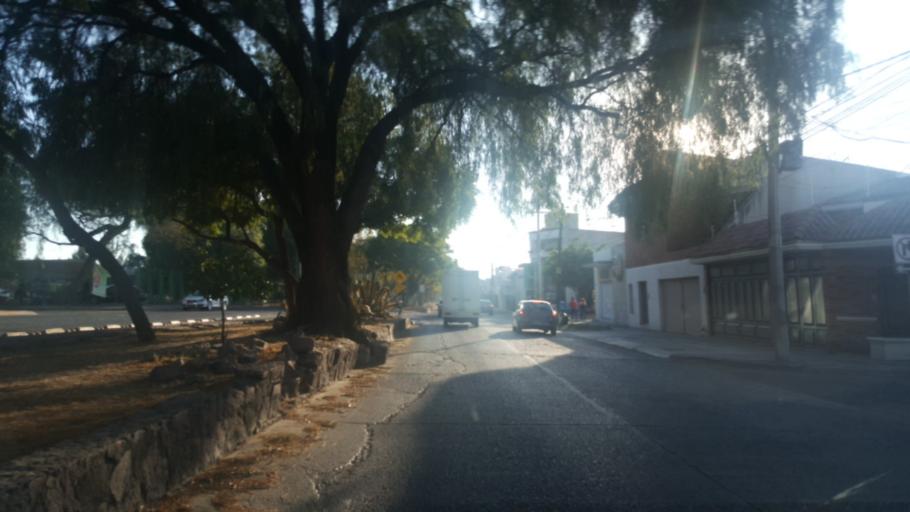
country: MX
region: Guanajuato
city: Leon
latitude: 21.1102
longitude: -101.6355
